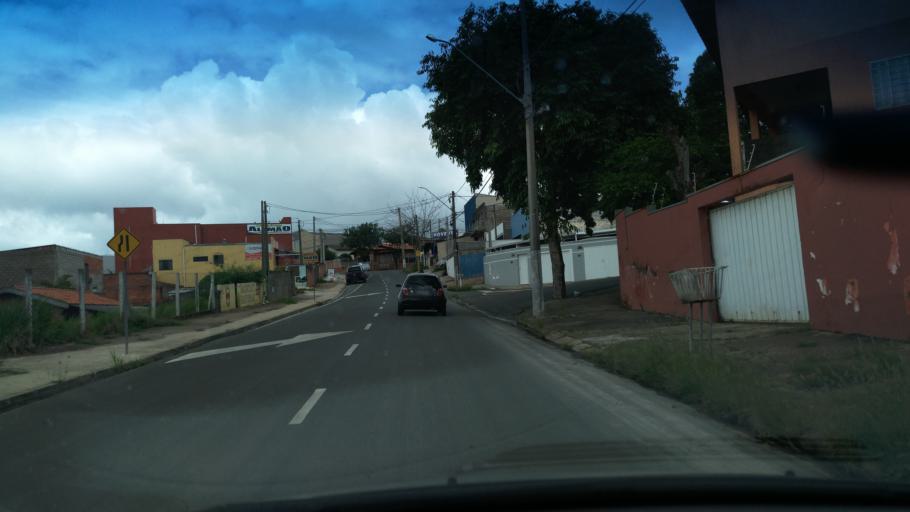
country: BR
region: Sao Paulo
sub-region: Valinhos
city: Valinhos
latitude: -22.9578
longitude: -47.0001
